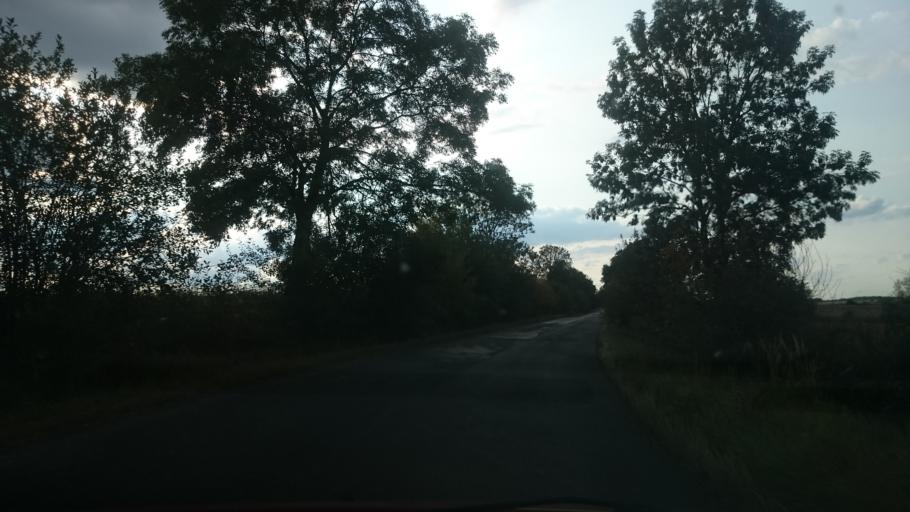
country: PL
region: Opole Voivodeship
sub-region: Powiat nyski
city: Otmuchow
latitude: 50.5005
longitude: 17.2041
